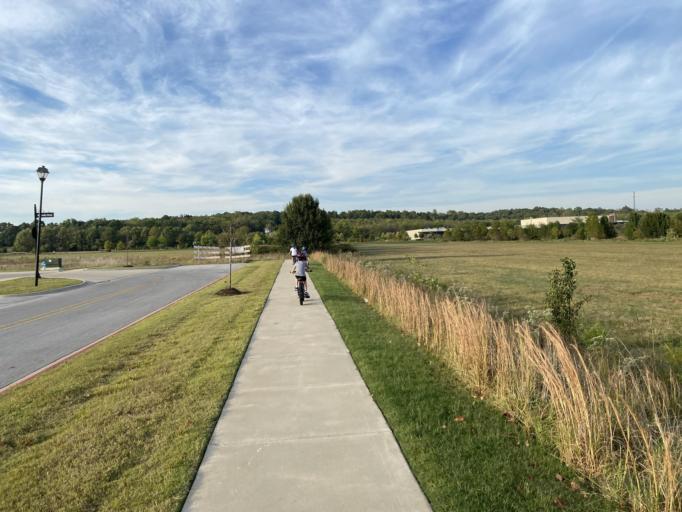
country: US
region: Arkansas
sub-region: Washington County
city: Johnson
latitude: 36.1117
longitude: -94.1853
